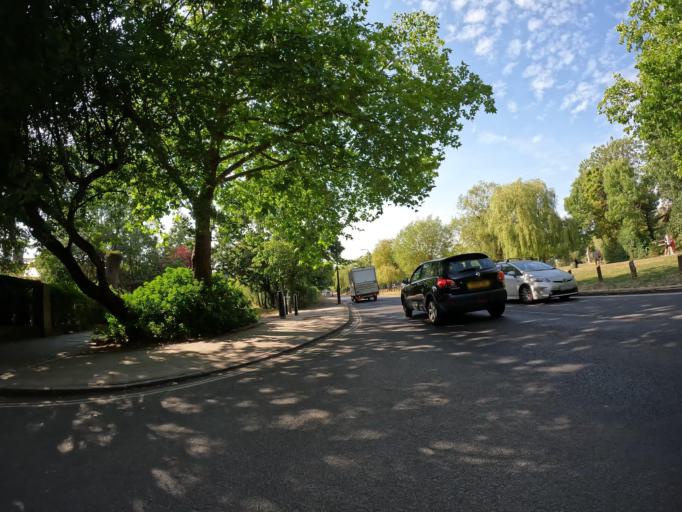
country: GB
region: England
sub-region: Greater London
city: Hadley Wood
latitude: 51.6627
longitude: -0.1706
